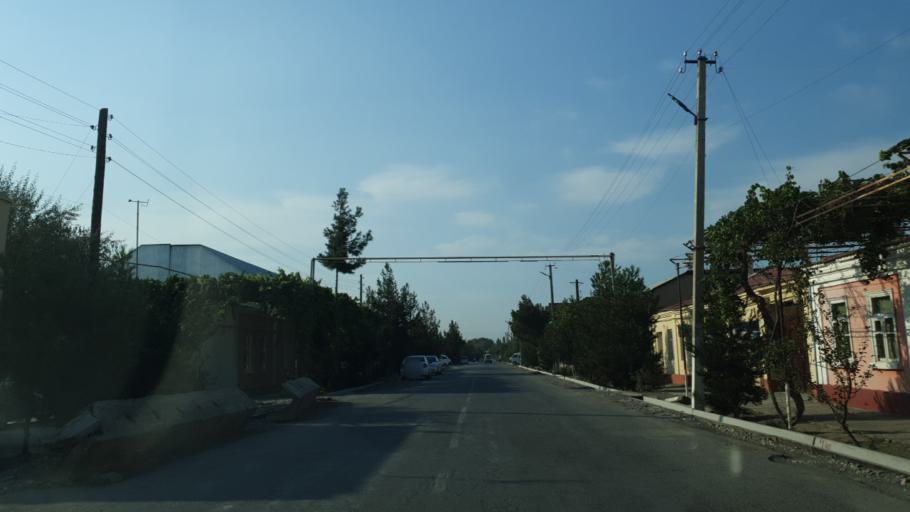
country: UZ
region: Fergana
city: Yaypan
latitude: 40.3714
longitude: 70.8133
